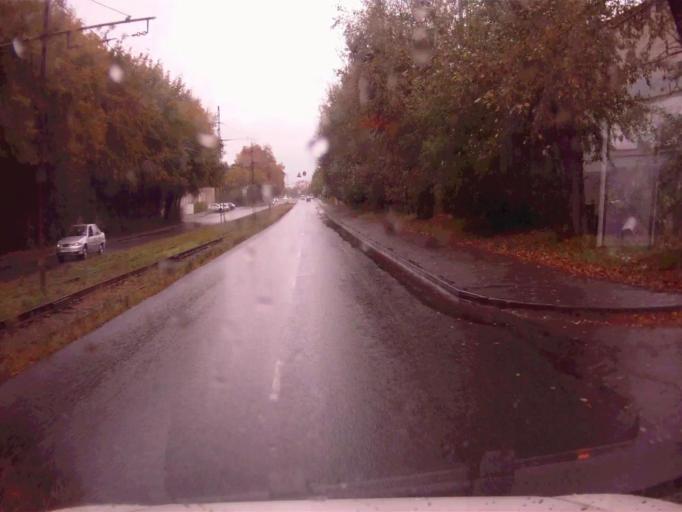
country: RU
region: Chelyabinsk
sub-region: Gorod Chelyabinsk
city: Chelyabinsk
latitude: 55.1793
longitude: 61.4148
